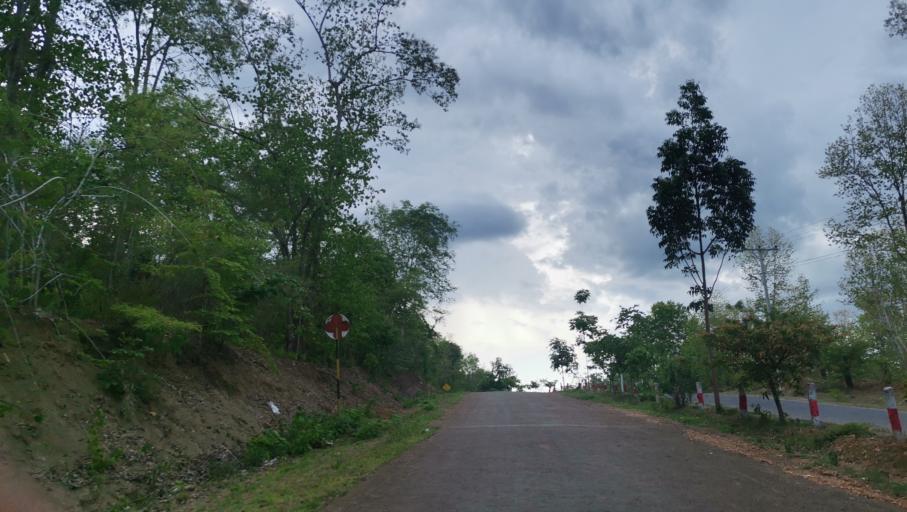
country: MM
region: Magway
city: Minbu
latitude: 20.1002
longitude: 94.5531
